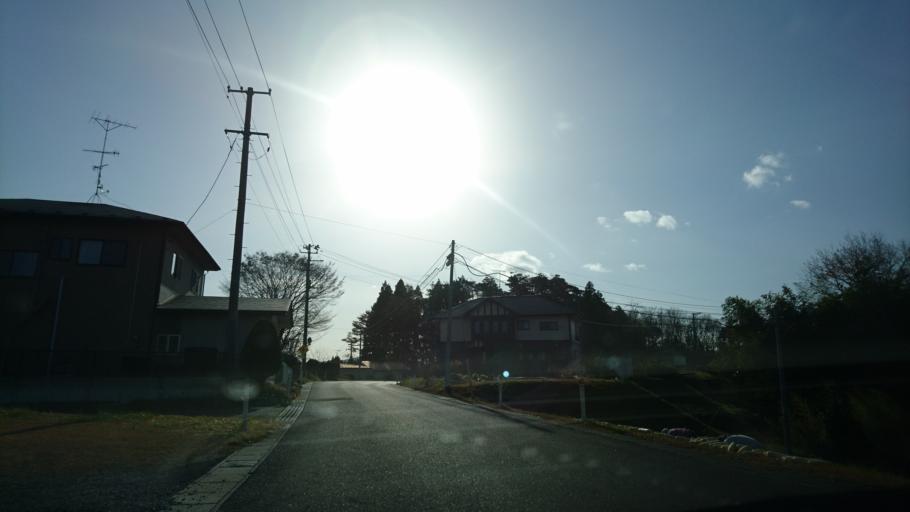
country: JP
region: Iwate
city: Ichinoseki
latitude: 38.9136
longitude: 141.3388
